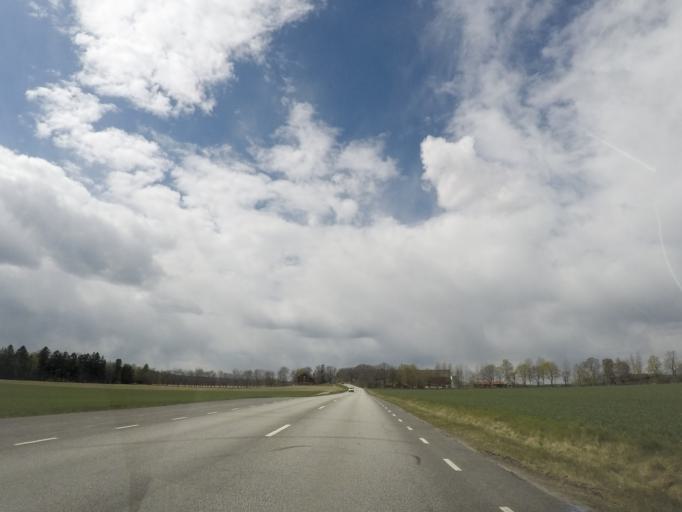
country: SE
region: Soedermanland
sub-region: Nykopings Kommun
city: Svalsta
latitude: 58.7414
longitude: 16.8132
